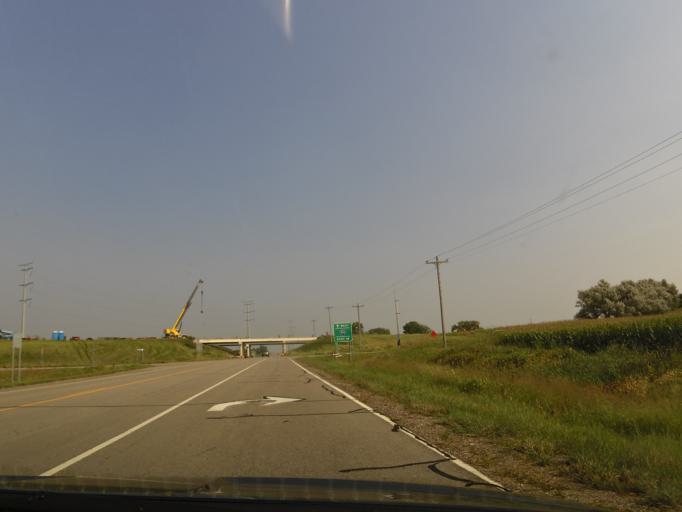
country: US
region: Minnesota
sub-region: Grant County
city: Elbow Lake
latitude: 45.9987
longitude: -95.7322
